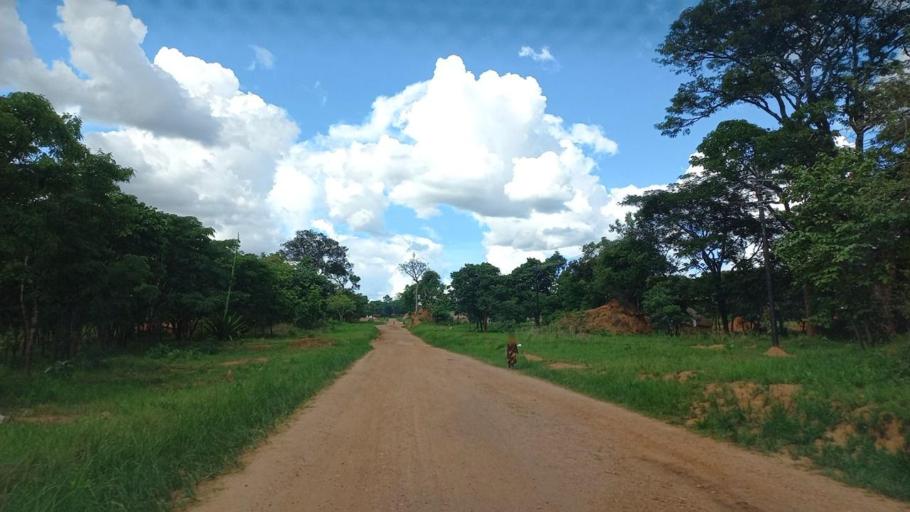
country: ZM
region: North-Western
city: Mwinilunga
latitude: -12.0729
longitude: 24.3011
